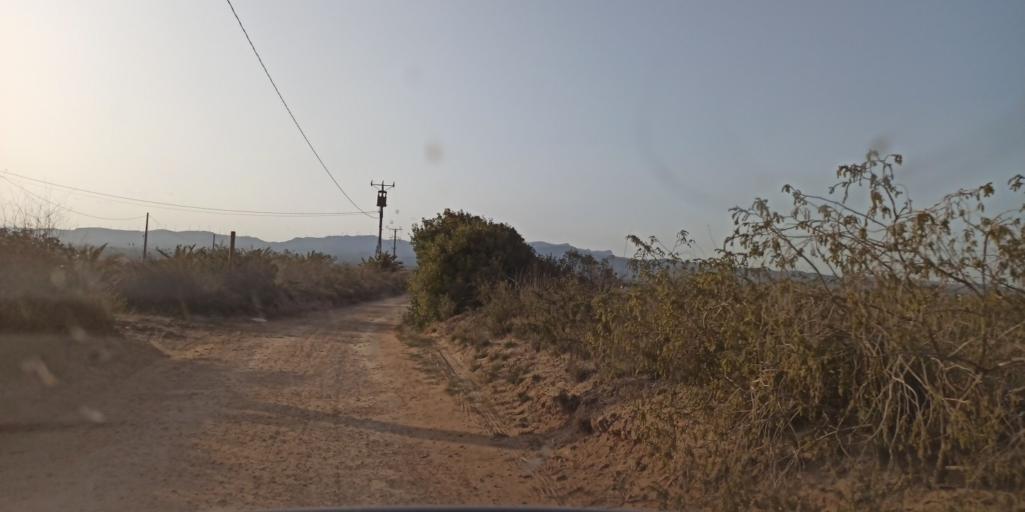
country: ES
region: Catalonia
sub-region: Provincia de Tarragona
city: L'Ampolla
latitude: 40.7842
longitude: 0.7112
